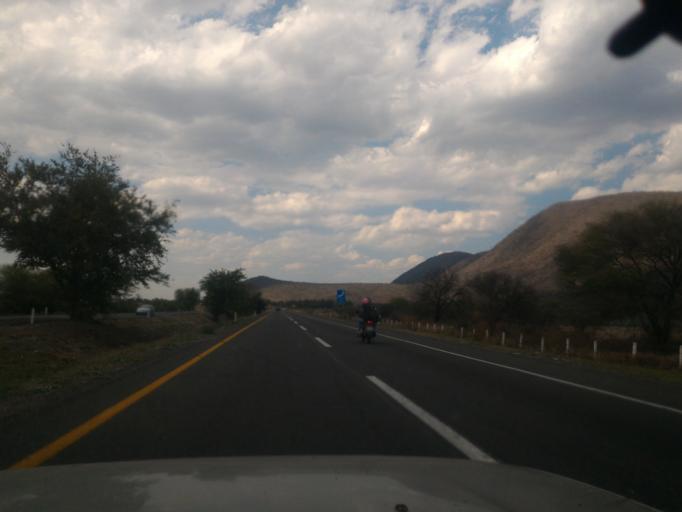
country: MX
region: Jalisco
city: Zacoalco de Torres
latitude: 20.1773
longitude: -103.5098
